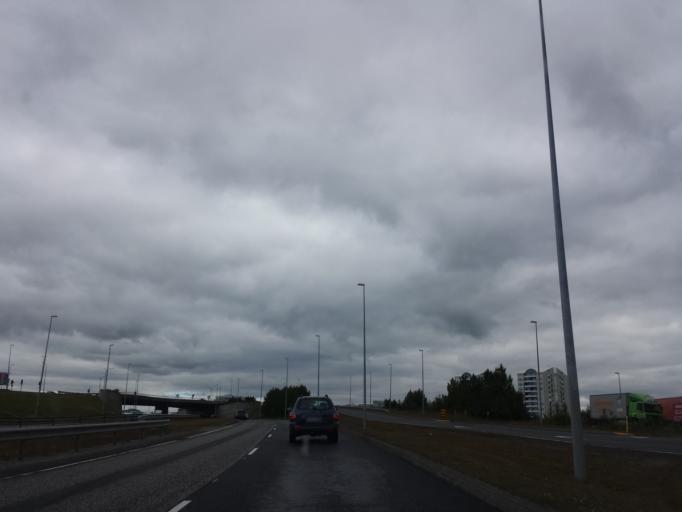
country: IS
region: Capital Region
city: Reykjavik
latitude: 64.1057
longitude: -21.8543
